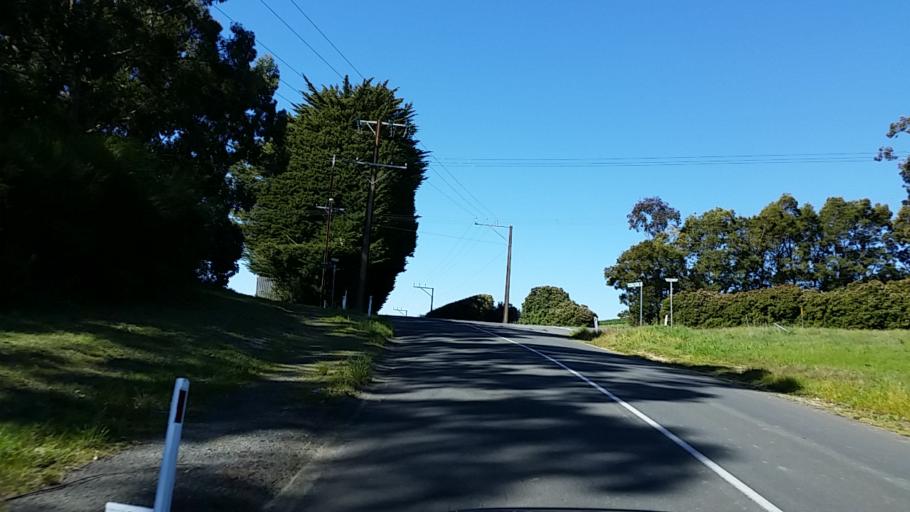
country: AU
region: South Australia
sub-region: Adelaide Hills
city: Bridgewater
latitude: -34.9558
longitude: 138.7542
